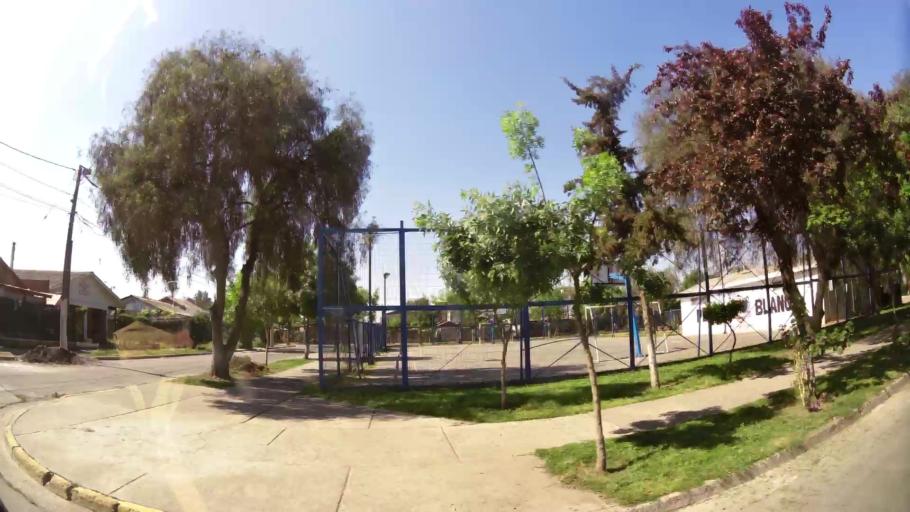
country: CL
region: Santiago Metropolitan
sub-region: Provincia de Talagante
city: Penaflor
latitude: -33.5666
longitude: -70.8082
